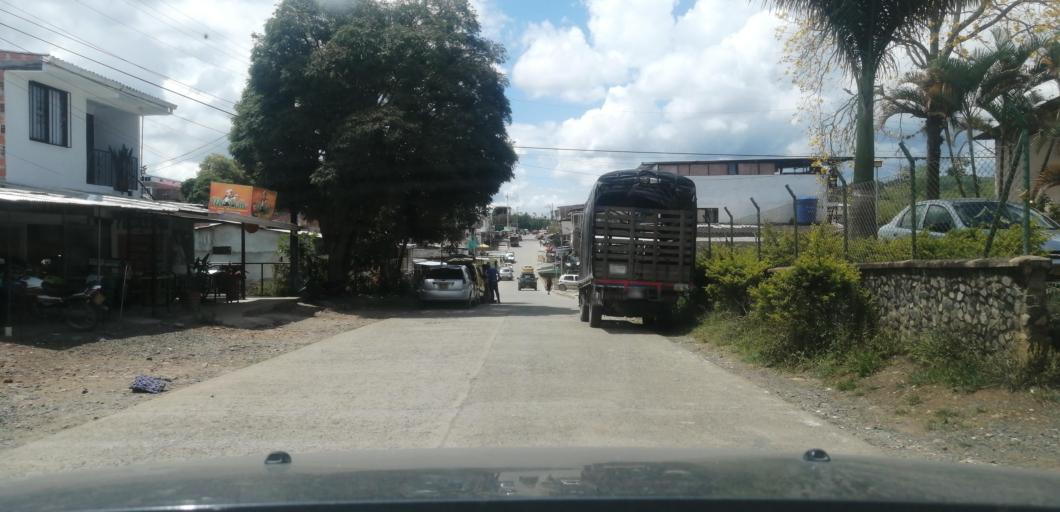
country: CO
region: Valle del Cauca
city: Restrepo
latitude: 3.8211
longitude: -76.5255
